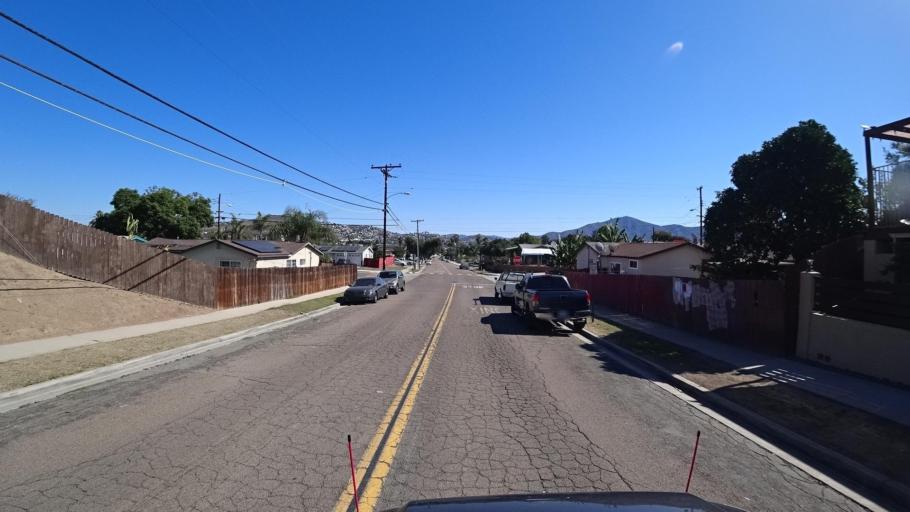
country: US
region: California
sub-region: San Diego County
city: La Presa
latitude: 32.7045
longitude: -117.0177
